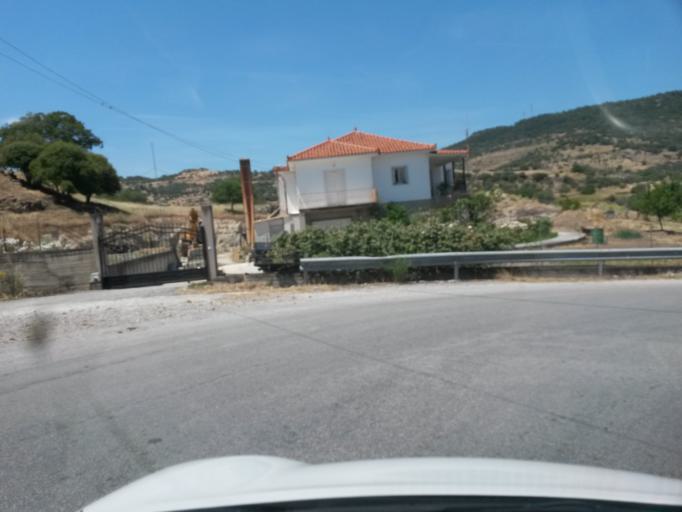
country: GR
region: North Aegean
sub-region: Nomos Lesvou
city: Mantamados
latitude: 39.3068
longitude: 26.3362
